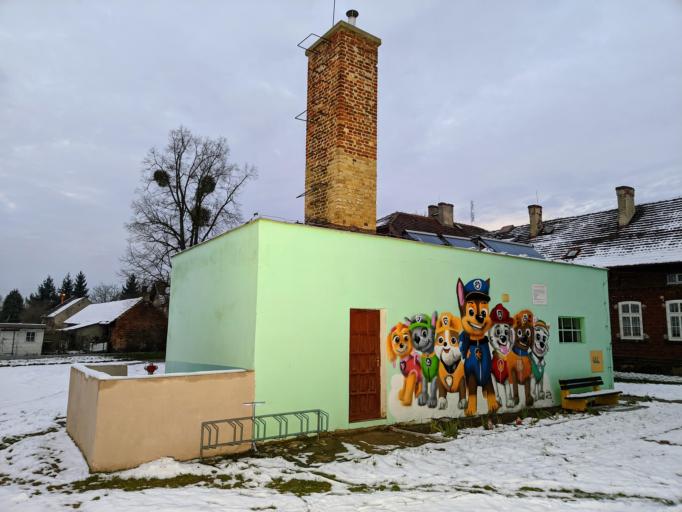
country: PL
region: Lower Silesian Voivodeship
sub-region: Powiat polkowicki
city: Przemkow
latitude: 51.5420
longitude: 15.7611
